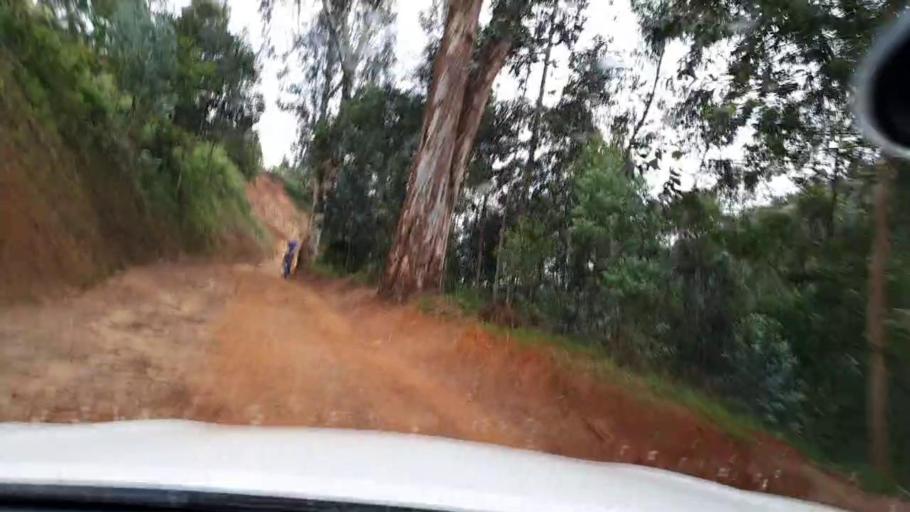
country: RW
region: Western Province
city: Cyangugu
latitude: -2.3988
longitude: 29.2311
